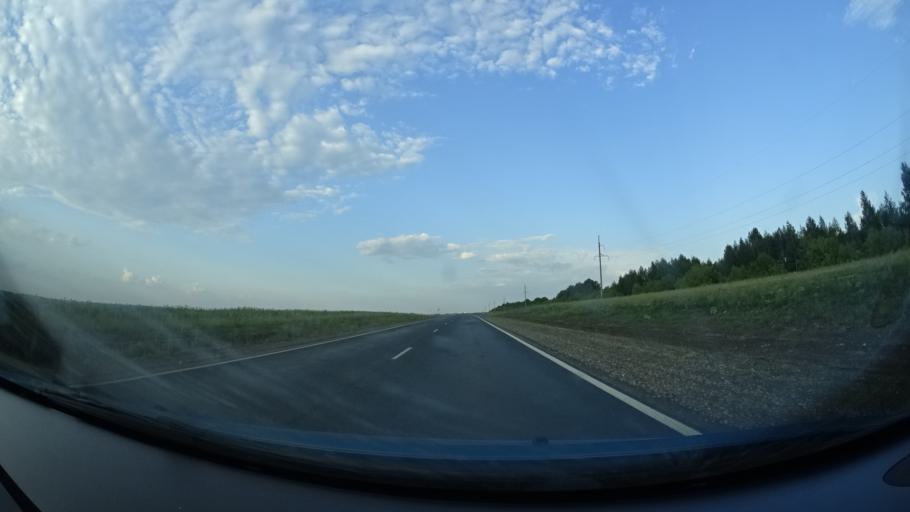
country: RU
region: Samara
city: Kamyshla
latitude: 54.0306
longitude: 51.9107
